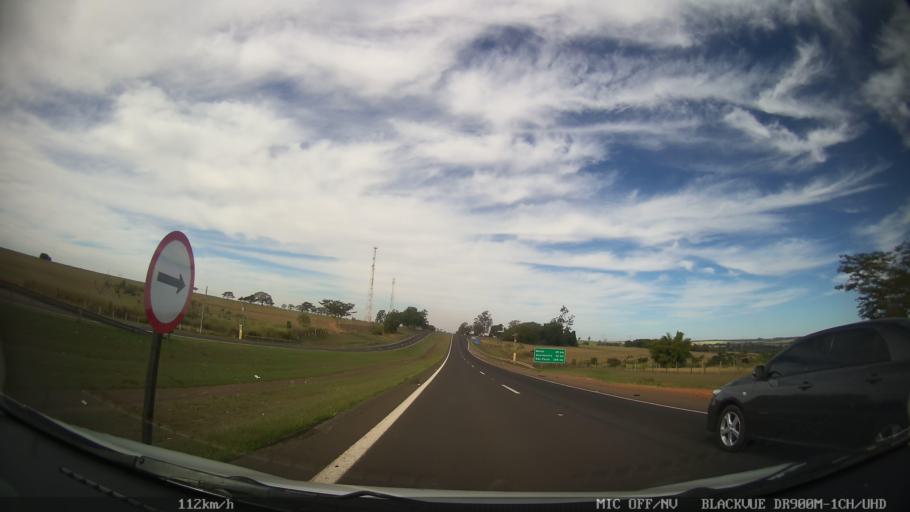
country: BR
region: Sao Paulo
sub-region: Taquaritinga
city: Taquaritinga
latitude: -21.5334
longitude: -48.5149
